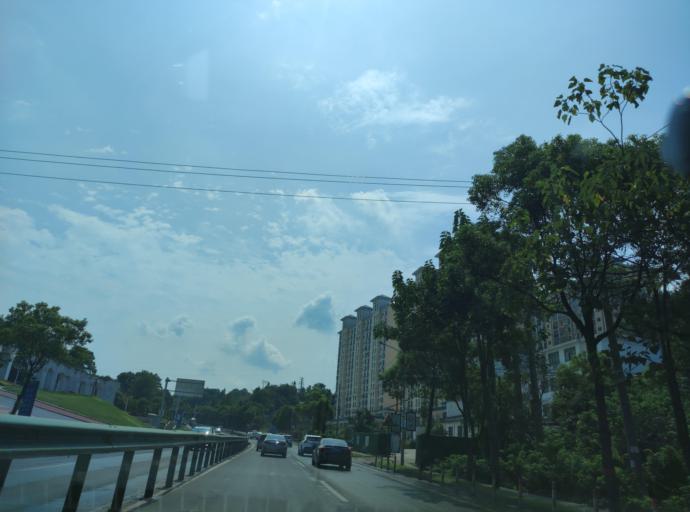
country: CN
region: Jiangxi Sheng
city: Pingxiang
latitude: 27.6519
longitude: 113.9171
